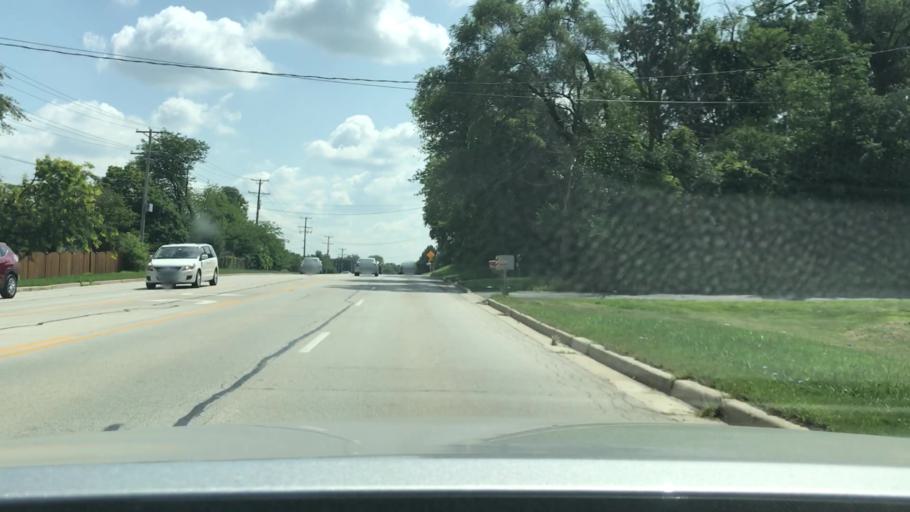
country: US
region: Illinois
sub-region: DuPage County
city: Woodridge
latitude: 41.7291
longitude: -88.0185
